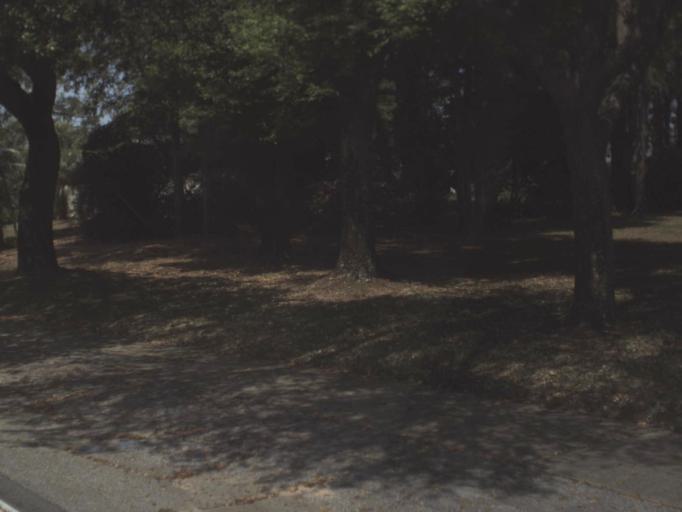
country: US
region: Florida
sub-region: Escambia County
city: East Pensacola Heights
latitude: 30.4488
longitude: -87.1880
